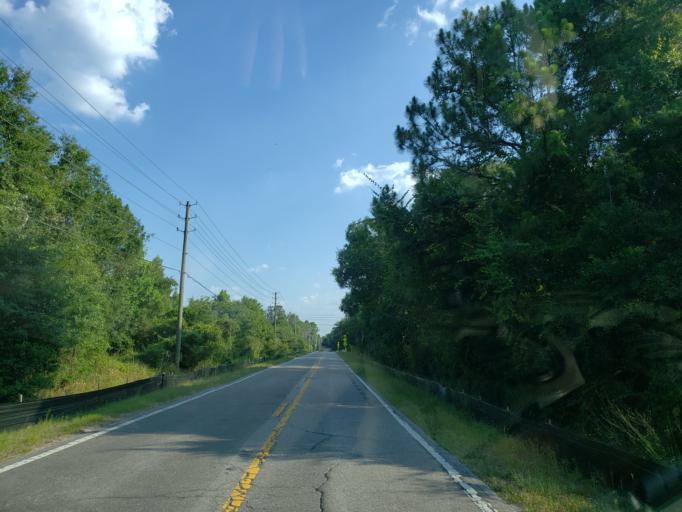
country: US
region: Florida
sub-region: Hillsborough County
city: Fish Hawk
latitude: 27.8567
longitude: -82.1988
